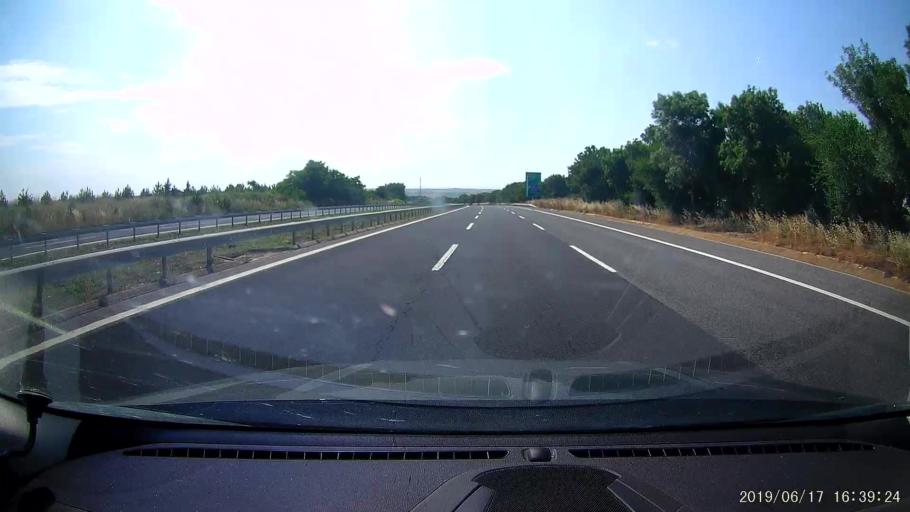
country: TR
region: Kirklareli
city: Luleburgaz
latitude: 41.4488
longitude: 27.4120
